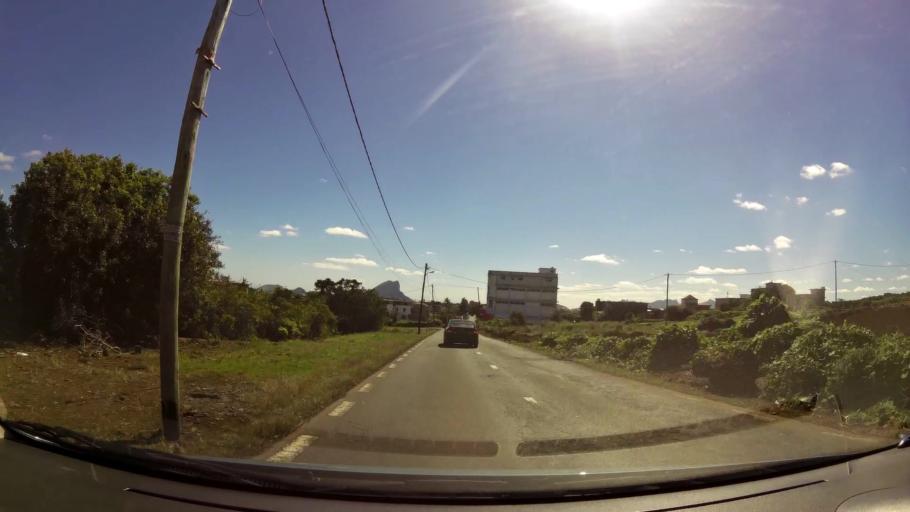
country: MU
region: Plaines Wilhems
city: Vacoas
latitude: -20.3314
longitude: 57.4869
